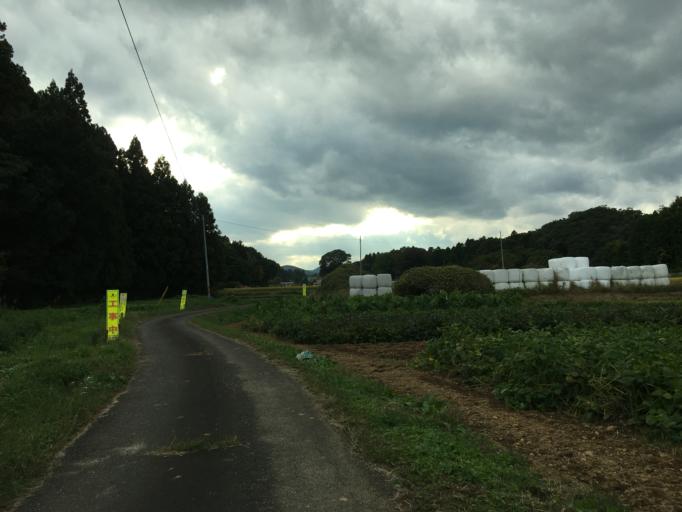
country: JP
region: Fukushima
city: Motomiya
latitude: 37.5561
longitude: 140.3792
